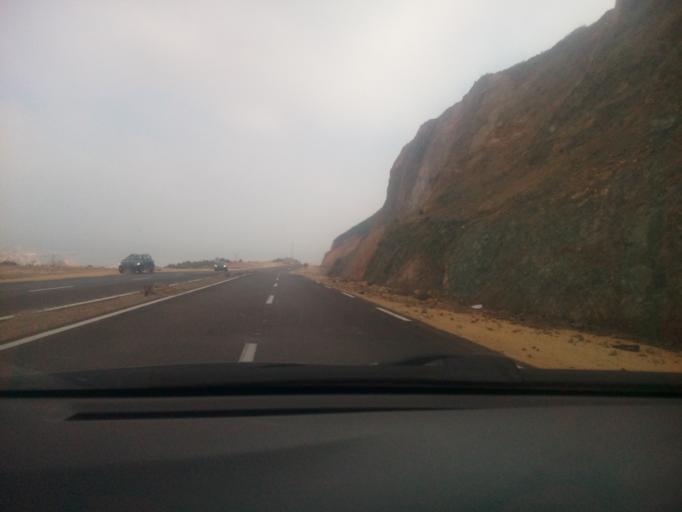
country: DZ
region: Oran
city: Mers el Kebir
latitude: 35.7164
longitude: -0.7276
